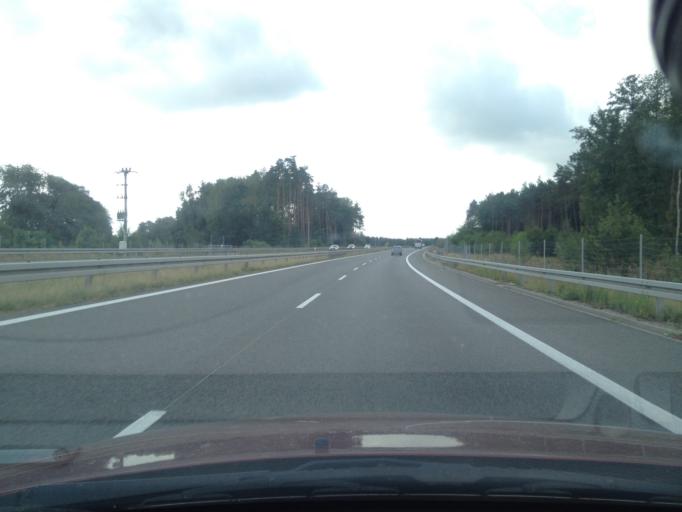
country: PL
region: West Pomeranian Voivodeship
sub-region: Powiat goleniowski
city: Goleniow
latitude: 53.6219
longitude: 14.8188
